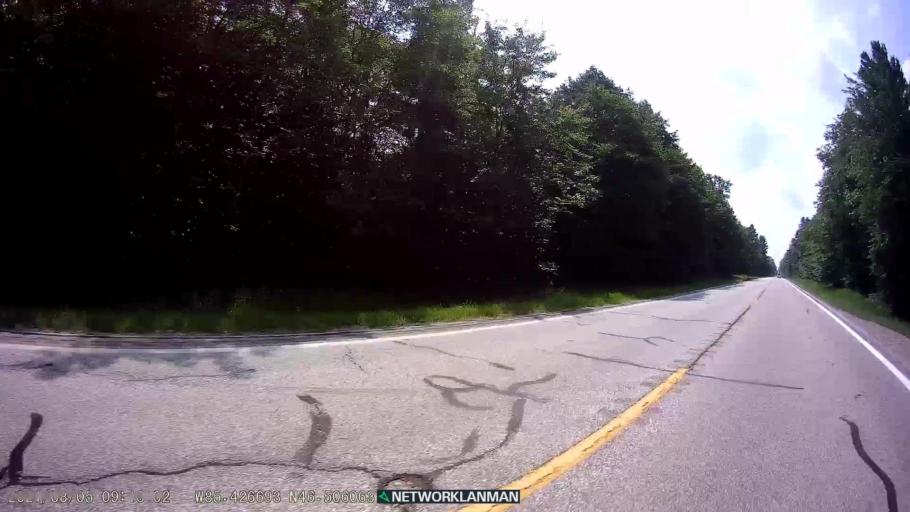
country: US
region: Michigan
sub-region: Luce County
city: Newberry
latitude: 46.5058
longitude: -85.4267
